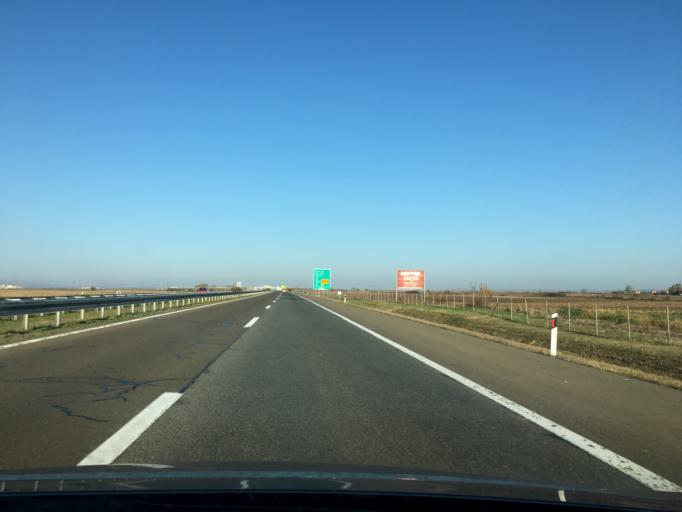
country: RS
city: Novi Karlovci
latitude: 45.0603
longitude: 20.1638
